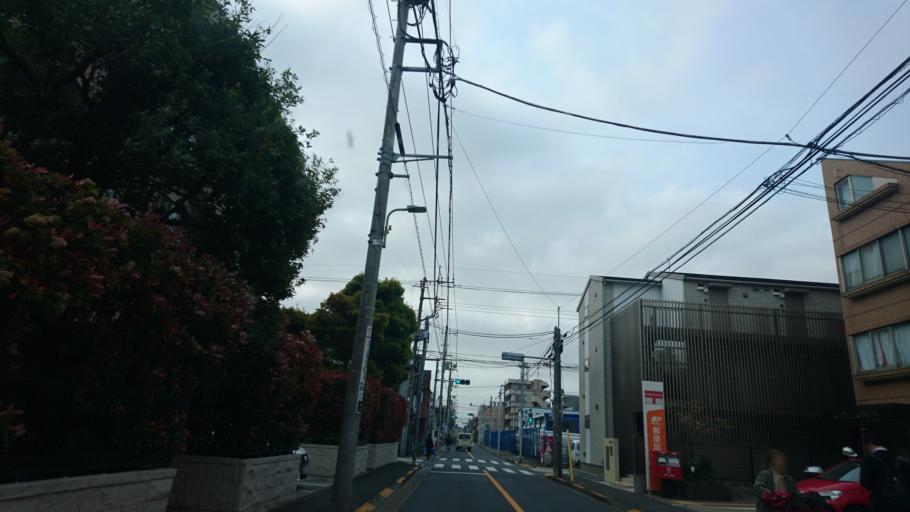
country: JP
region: Kanagawa
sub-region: Kawasaki-shi
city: Kawasaki
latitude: 35.5675
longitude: 139.7042
